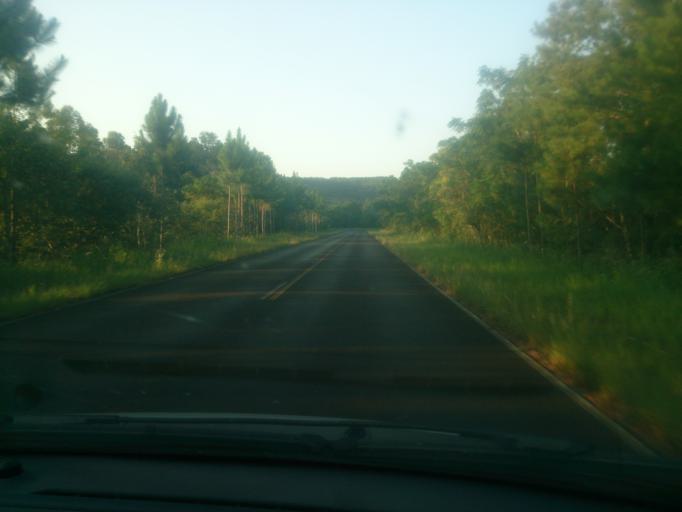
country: AR
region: Misiones
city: Panambi
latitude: -27.6704
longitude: -54.9125
